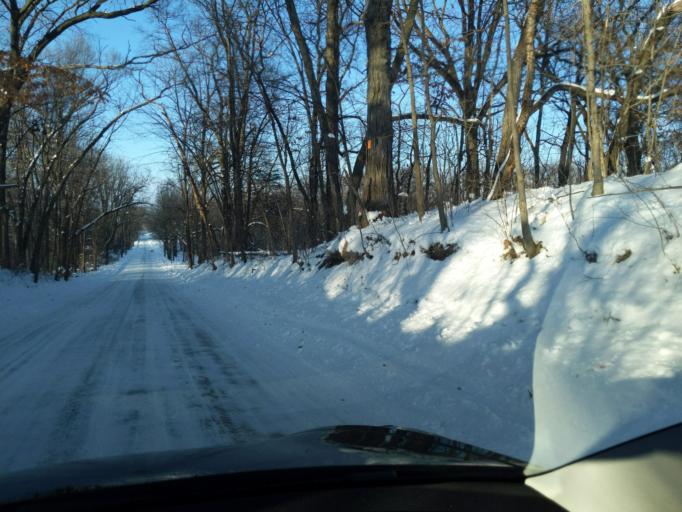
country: US
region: Michigan
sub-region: Ingham County
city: Stockbridge
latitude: 42.4766
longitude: -84.1199
